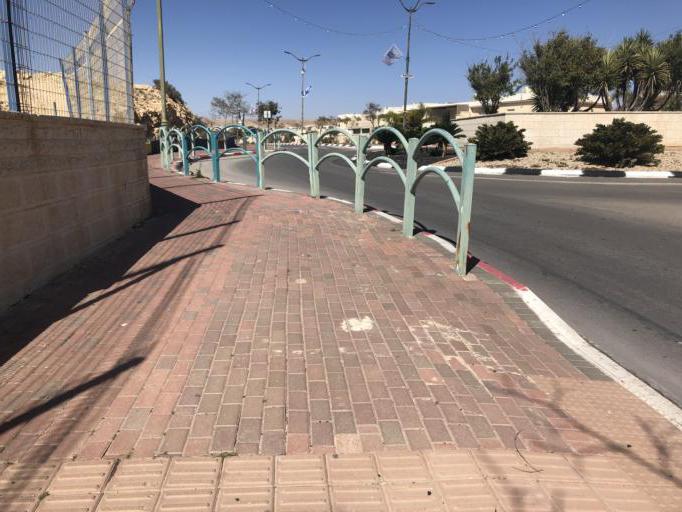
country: IL
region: Southern District
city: Dimona
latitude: 31.0681
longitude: 35.0397
